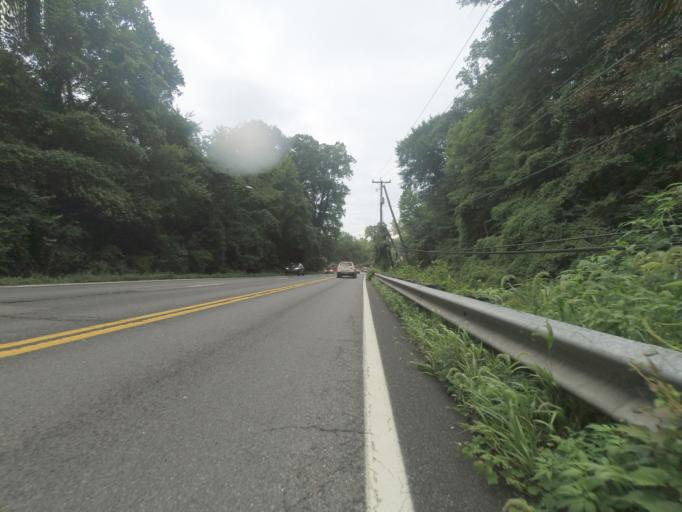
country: US
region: West Virginia
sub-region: Cabell County
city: Huntington
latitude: 38.4037
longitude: -82.4479
